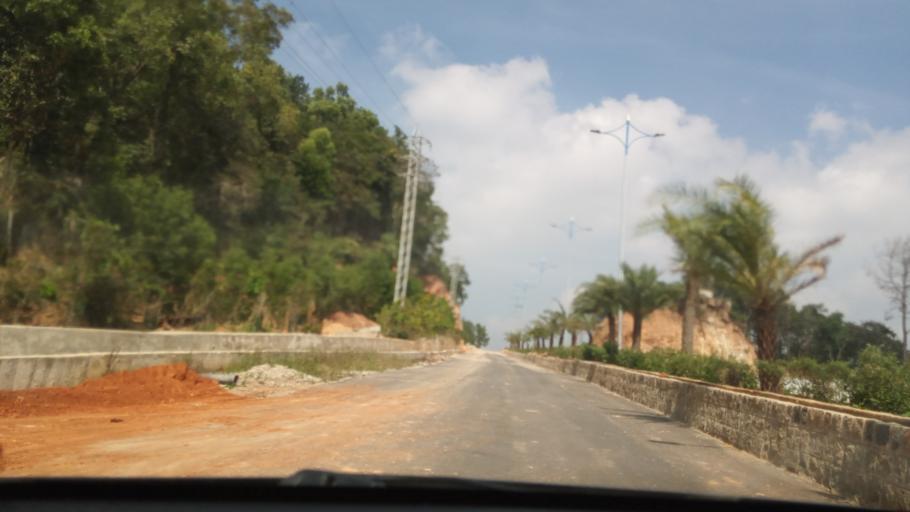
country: IN
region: Andhra Pradesh
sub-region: Chittoor
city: Tirumala
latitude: 13.6844
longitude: 79.3413
